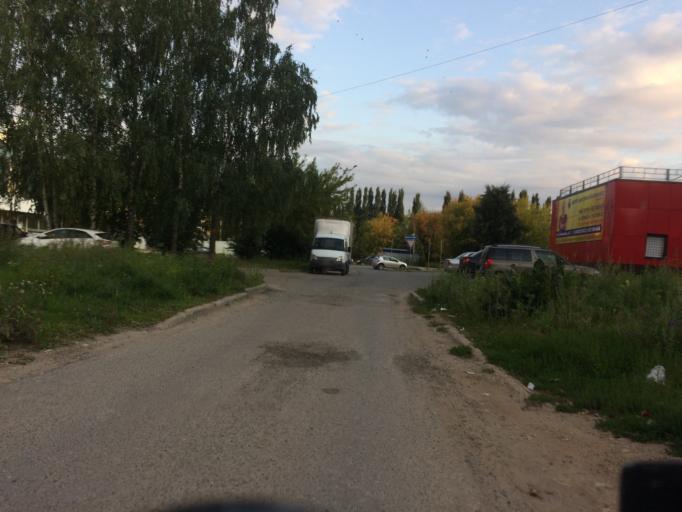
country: RU
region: Mariy-El
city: Yoshkar-Ola
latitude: 56.6424
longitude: 47.8495
